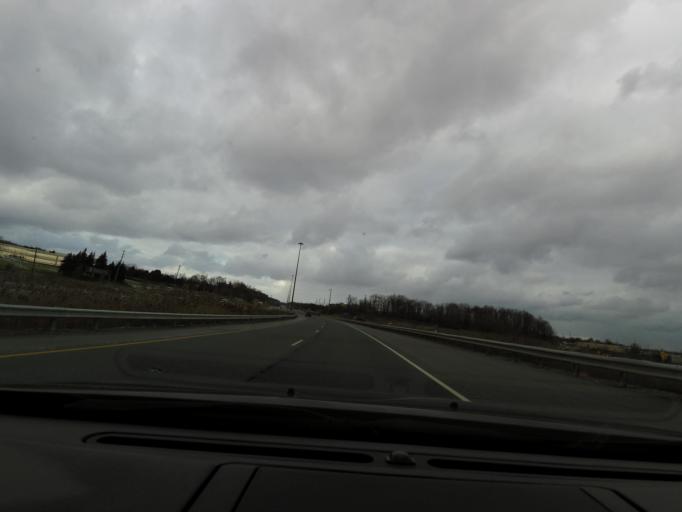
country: CA
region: Ontario
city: Burlington
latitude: 43.3391
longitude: -79.8309
